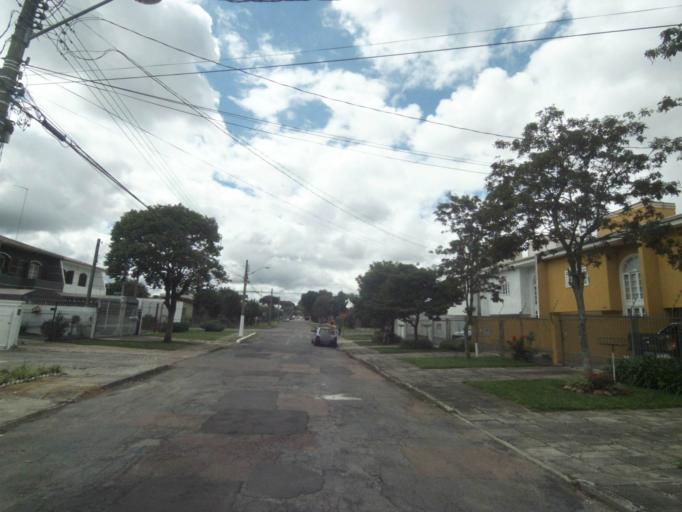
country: BR
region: Parana
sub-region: Curitiba
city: Curitiba
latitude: -25.4772
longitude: -49.2680
